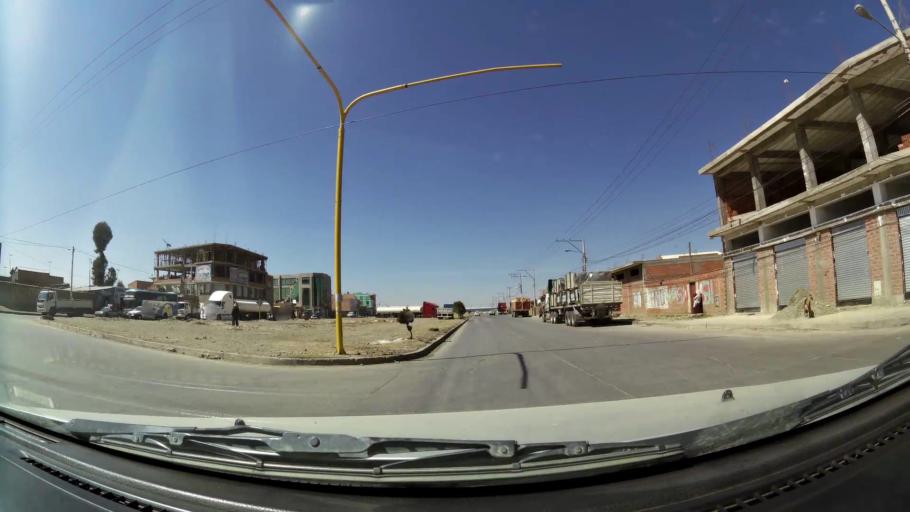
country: BO
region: La Paz
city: La Paz
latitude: -16.5512
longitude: -68.1876
